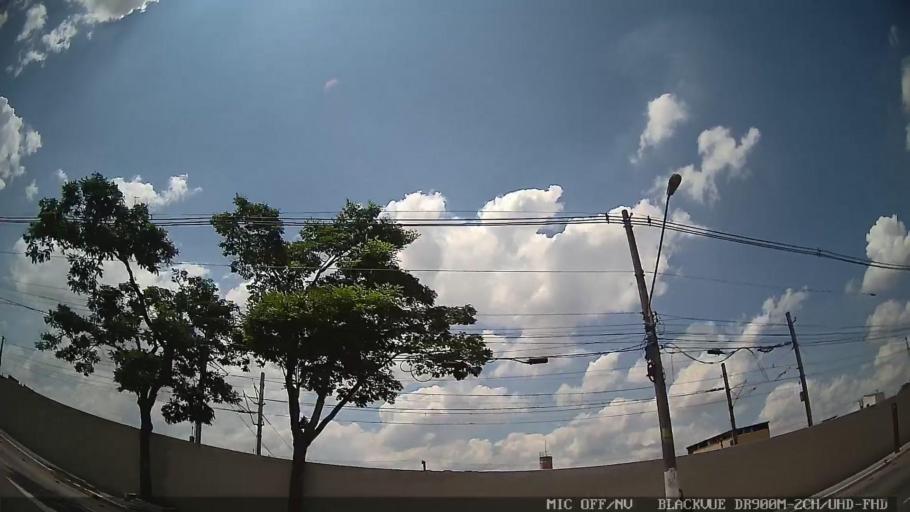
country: BR
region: Sao Paulo
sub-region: Guarulhos
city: Guarulhos
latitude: -23.4924
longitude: -46.4557
